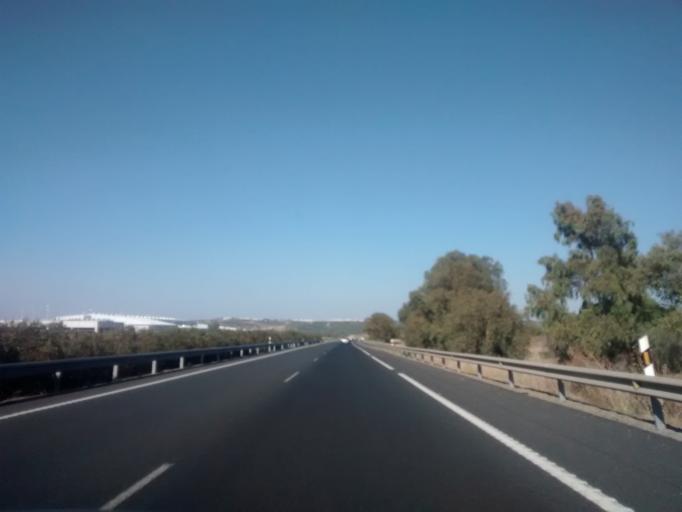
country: ES
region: Andalusia
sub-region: Provincia de Sevilla
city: Sanlucar la Mayor
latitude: 37.3648
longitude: -6.2571
